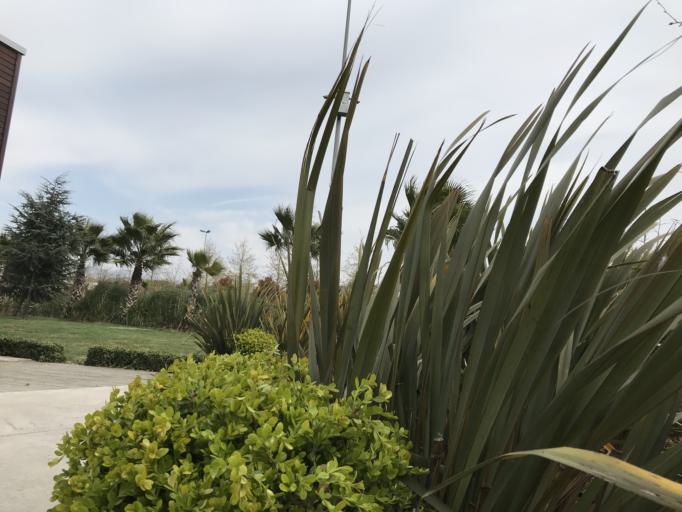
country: TR
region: Istanbul
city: Maltepe
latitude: 40.9382
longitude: 29.1100
